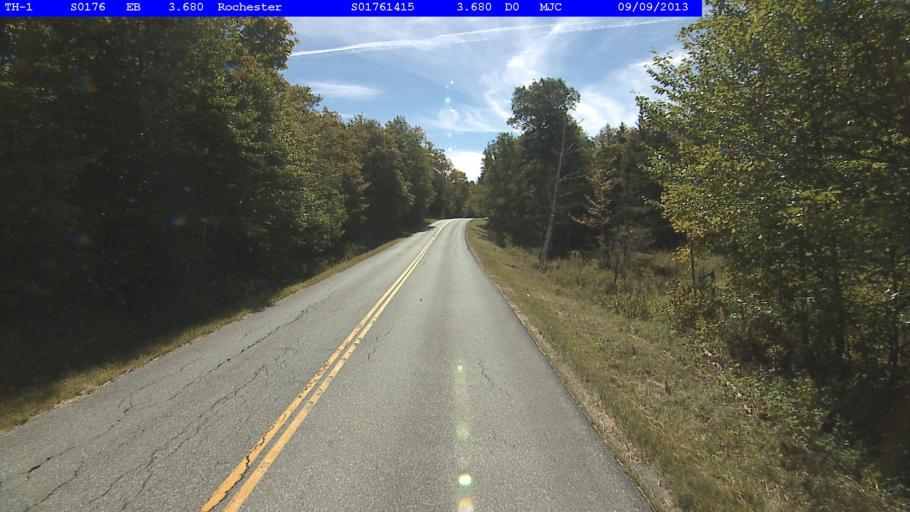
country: US
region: Vermont
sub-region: Orange County
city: Randolph
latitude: 43.8543
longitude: -72.7545
